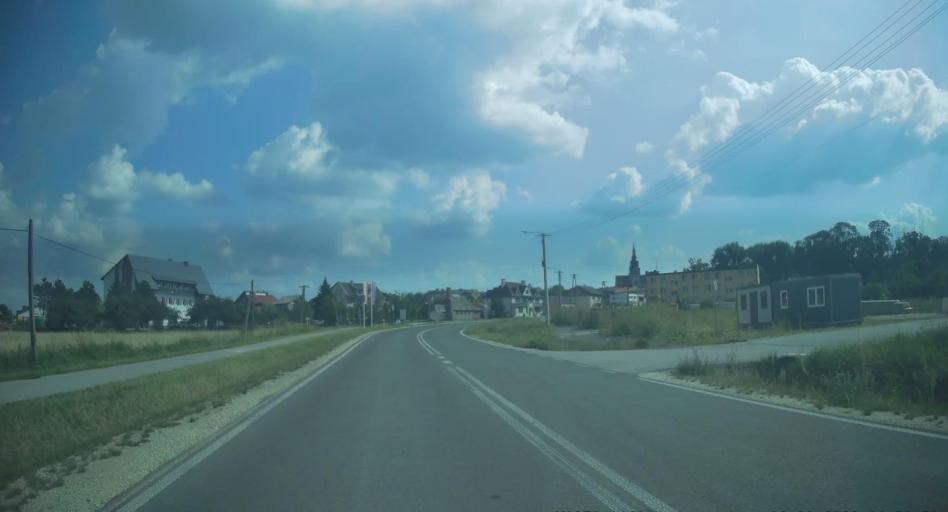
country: PL
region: Swietokrzyskie
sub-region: Powiat kielecki
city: Lopuszno
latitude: 50.9526
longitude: 20.2517
